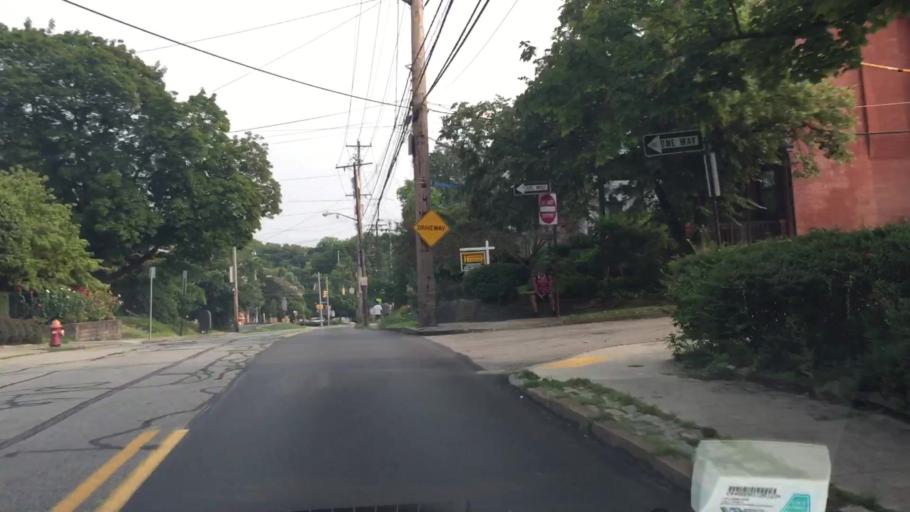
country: US
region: Pennsylvania
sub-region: Allegheny County
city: Bloomfield
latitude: 40.4532
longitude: -79.9440
